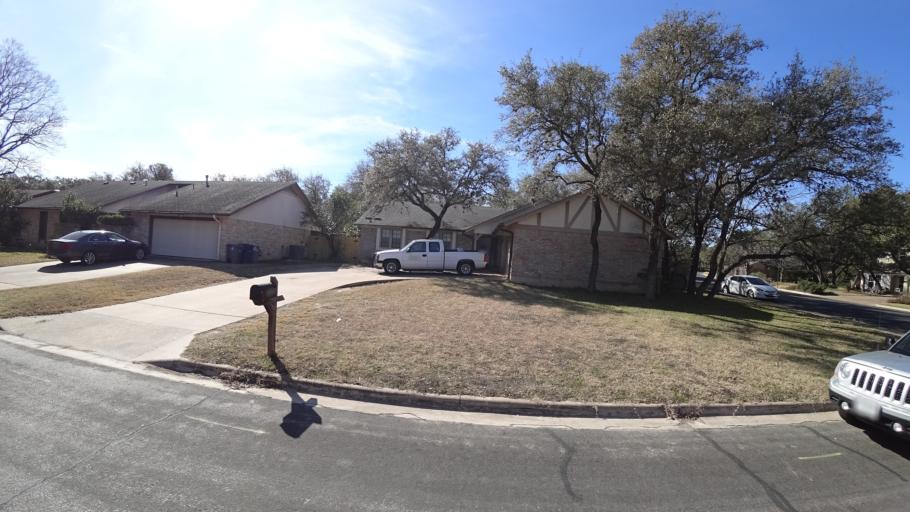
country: US
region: Texas
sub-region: Travis County
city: Wells Branch
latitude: 30.3884
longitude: -97.6924
